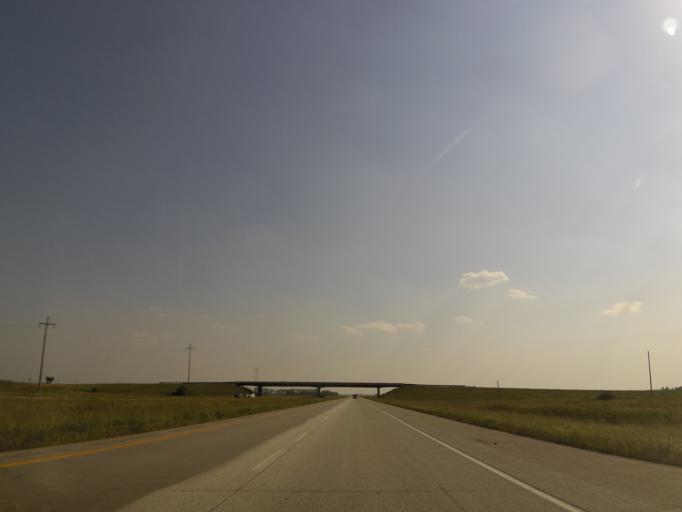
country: US
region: North Dakota
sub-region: Walsh County
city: Grafton
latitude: 48.3265
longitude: -97.1896
